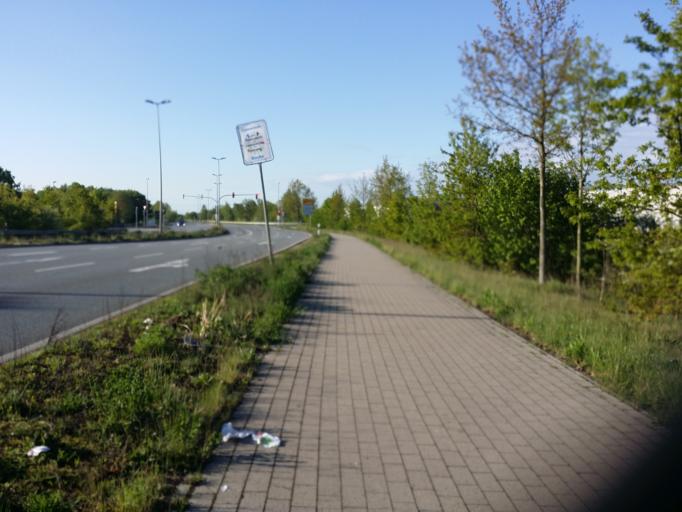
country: DE
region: Bremen
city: Bremen
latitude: 53.0218
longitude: 8.8659
